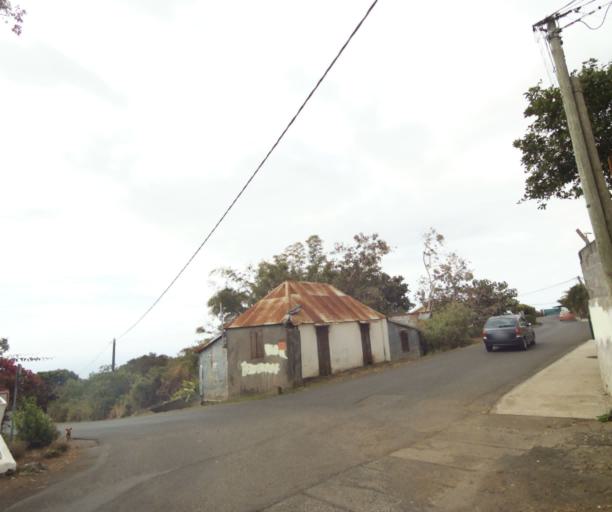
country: RE
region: Reunion
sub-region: Reunion
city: Saint-Paul
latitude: -21.0252
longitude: 55.3047
